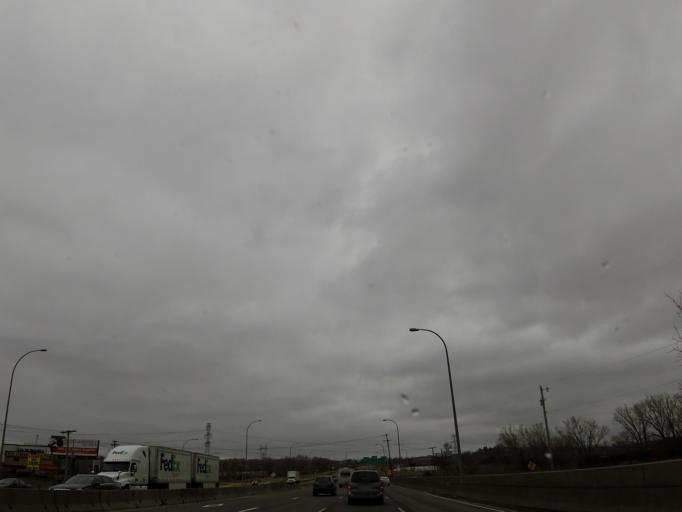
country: US
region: Minnesota
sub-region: Dakota County
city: Burnsville
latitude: 44.7876
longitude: -93.2887
